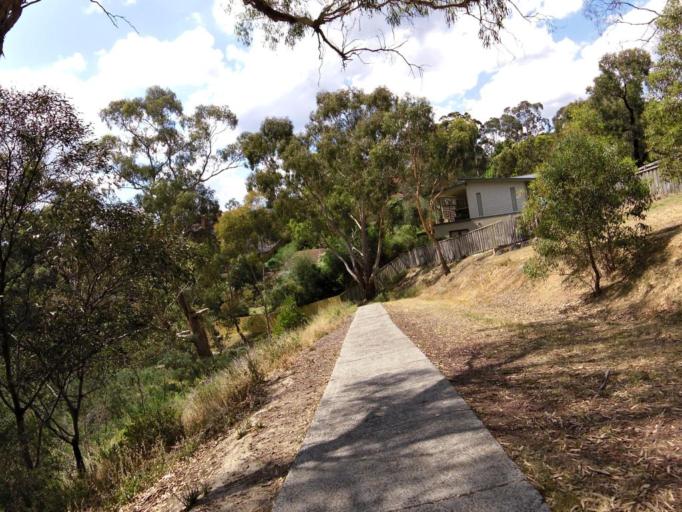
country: AU
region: Victoria
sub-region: Banyule
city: Greensborough
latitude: -37.6909
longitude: 145.1011
